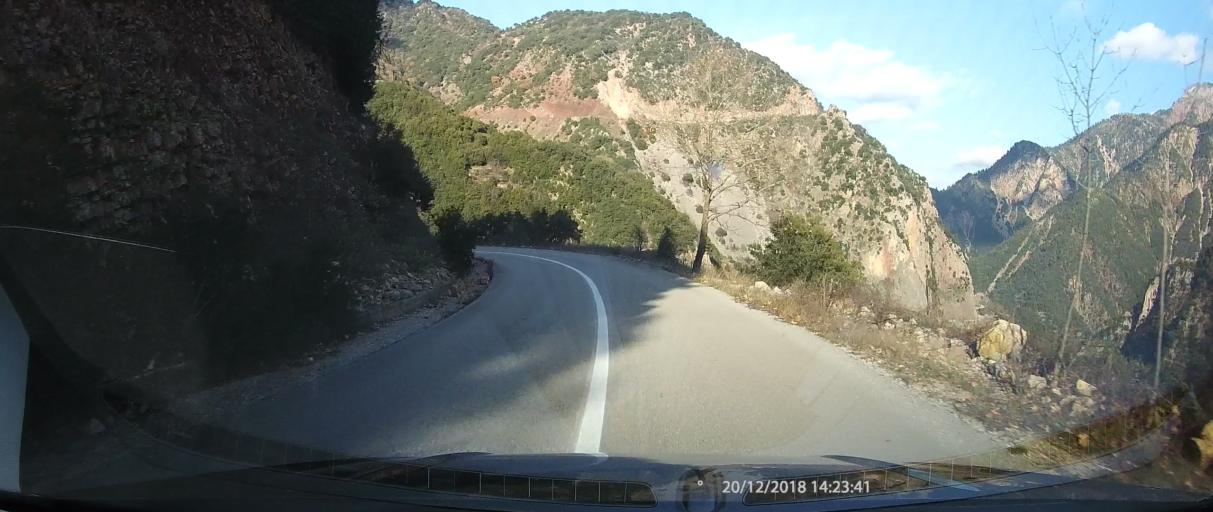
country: GR
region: West Greece
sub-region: Nomos Aitolias kai Akarnanias
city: Thermo
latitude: 38.7574
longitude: 21.6699
